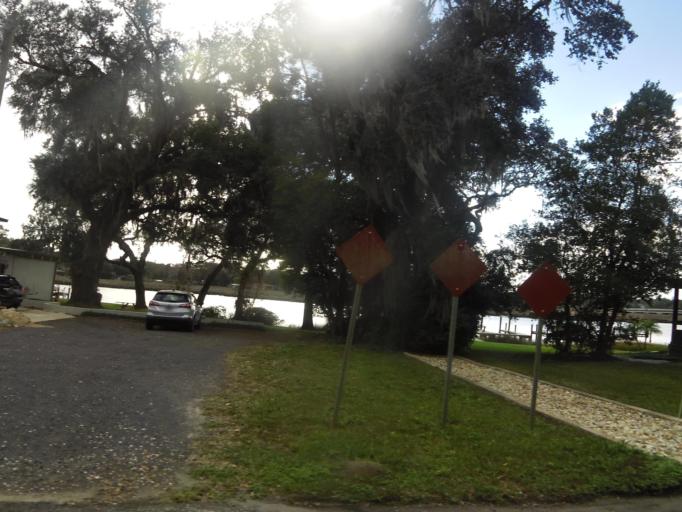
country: US
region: Florida
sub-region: Duval County
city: Jacksonville
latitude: 30.3219
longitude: -81.5922
